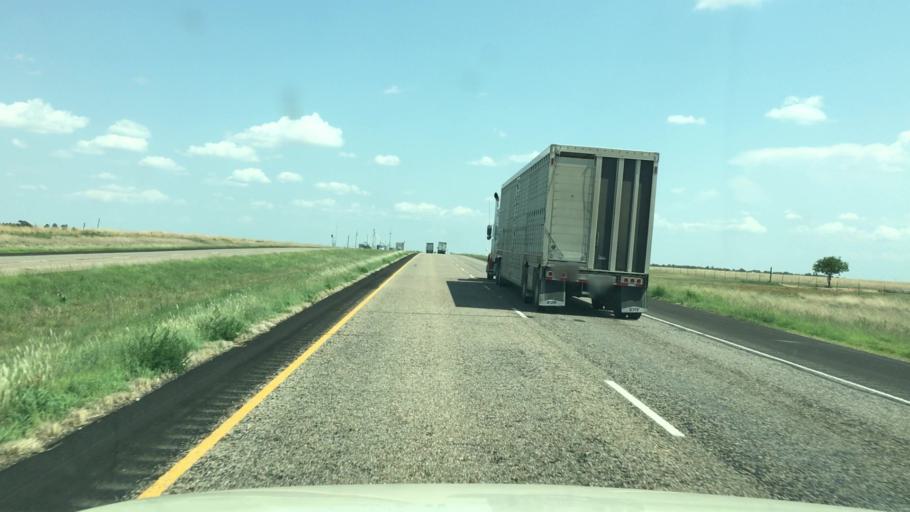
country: US
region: Texas
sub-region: Armstrong County
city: Claude
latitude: 35.1243
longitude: -101.3942
